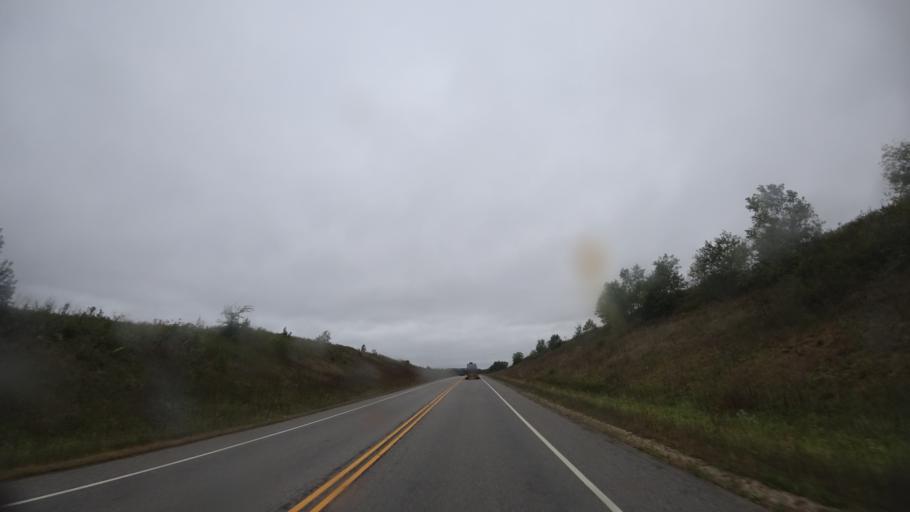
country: US
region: Wisconsin
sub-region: Crawford County
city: Prairie du Chien
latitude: 43.0208
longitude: -91.0314
